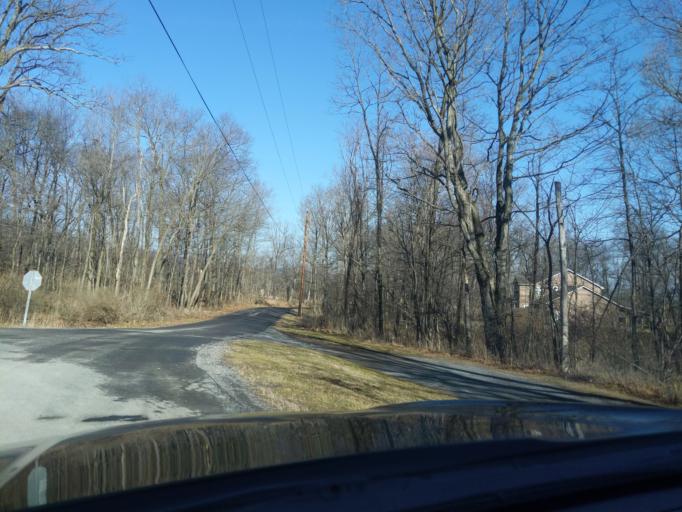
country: US
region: Pennsylvania
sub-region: Blair County
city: Bellwood
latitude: 40.5785
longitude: -78.2735
